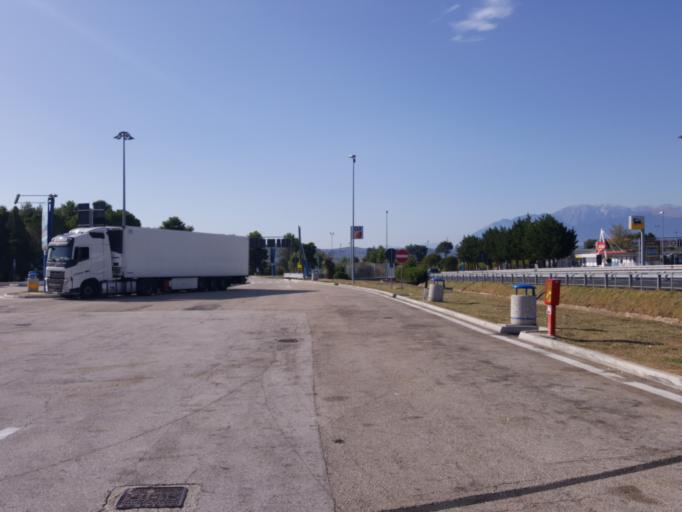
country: IT
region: Abruzzo
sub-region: Provincia di Chieti
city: Miglianico
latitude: 42.3884
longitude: 14.2890
